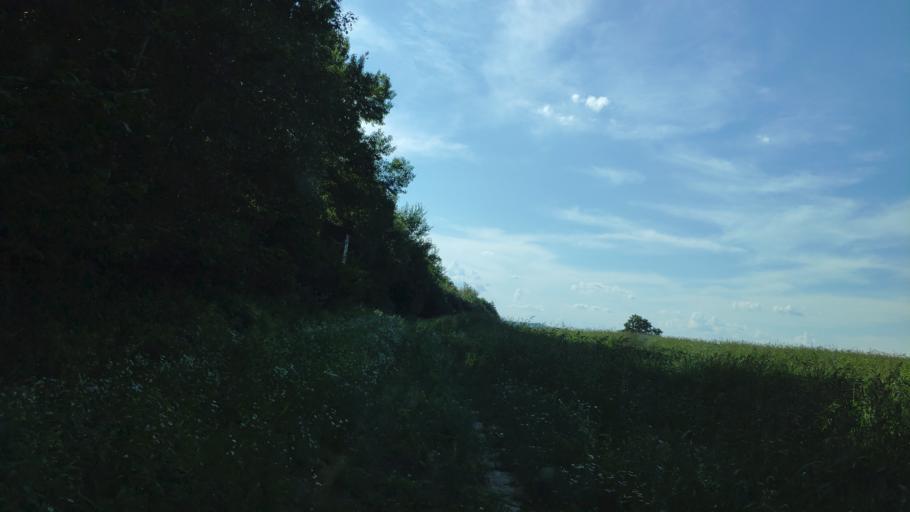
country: SK
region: Presovsky
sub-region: Okres Presov
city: Presov
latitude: 48.9057
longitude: 21.2963
